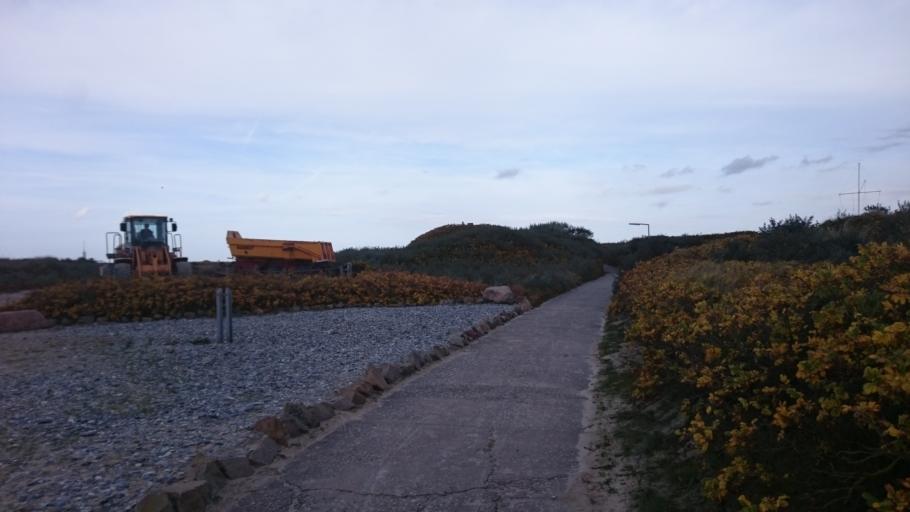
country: DE
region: Schleswig-Holstein
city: Helgoland
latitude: 54.1837
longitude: 7.9107
